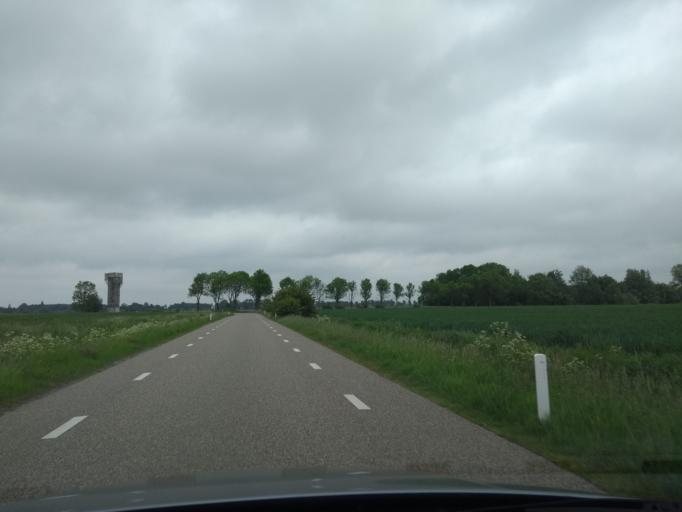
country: NL
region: Groningen
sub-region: Gemeente Zuidhorn
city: Oldehove
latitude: 53.3458
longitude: 6.4247
